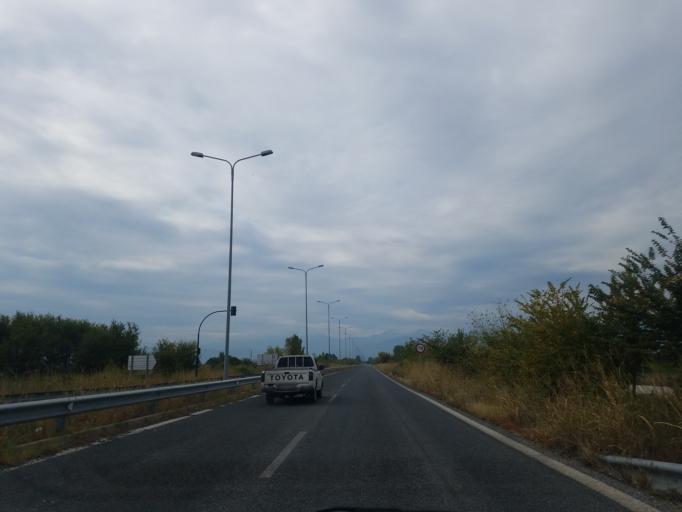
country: GR
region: Thessaly
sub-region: Trikala
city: Pyrgetos
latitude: 39.5657
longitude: 21.7385
